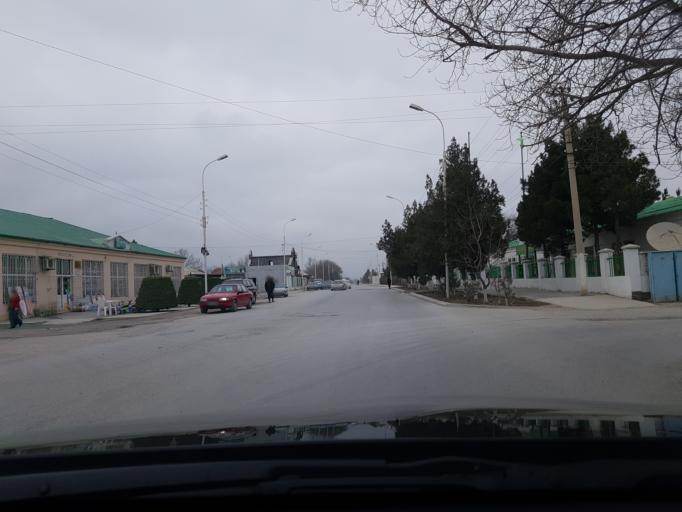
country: TM
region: Ahal
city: Abadan
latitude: 38.1572
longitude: 57.9612
